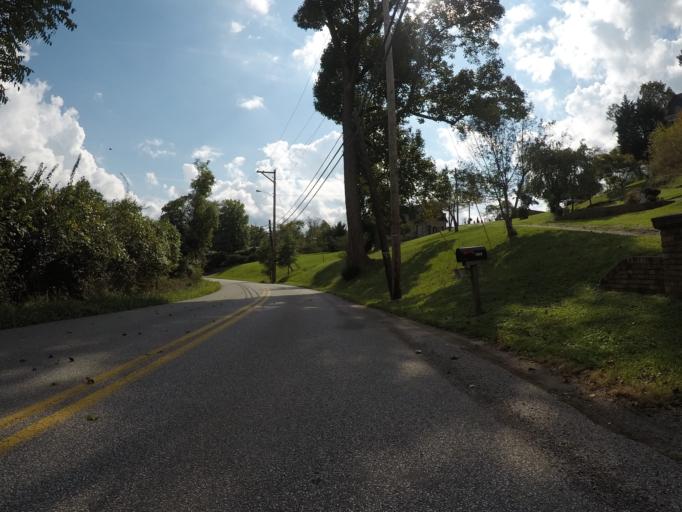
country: US
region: West Virginia
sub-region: Cabell County
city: Huntington
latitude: 38.3977
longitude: -82.4343
